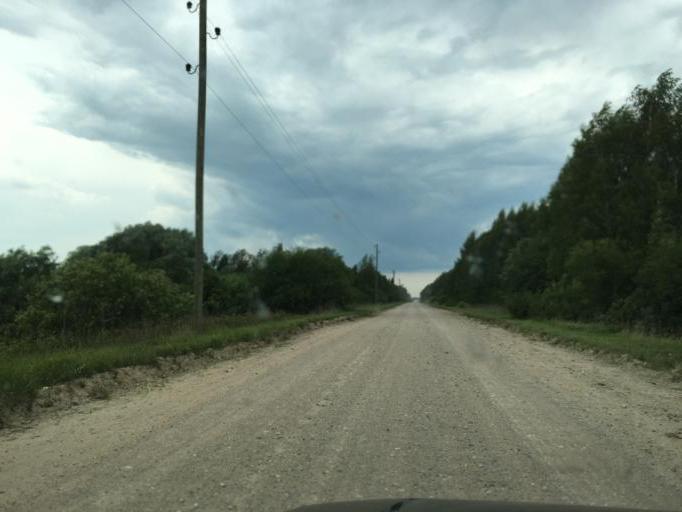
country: LV
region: Lubana
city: Lubana
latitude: 56.8237
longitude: 26.8877
